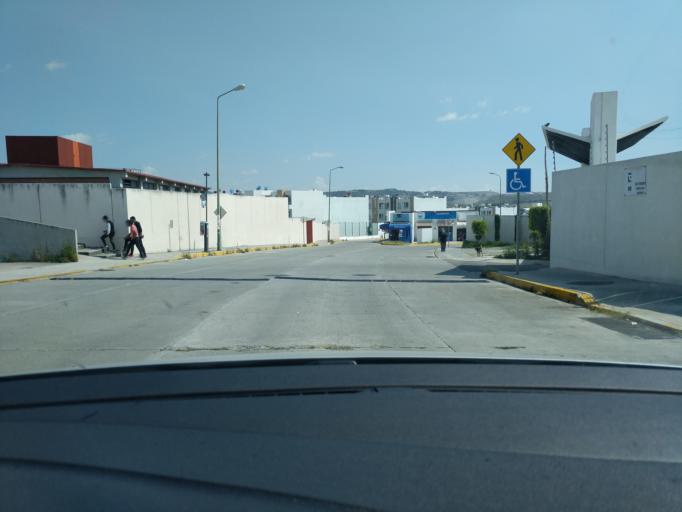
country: MX
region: Puebla
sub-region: Puebla
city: Galaxia la Calera
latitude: 19.0034
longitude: -98.1479
